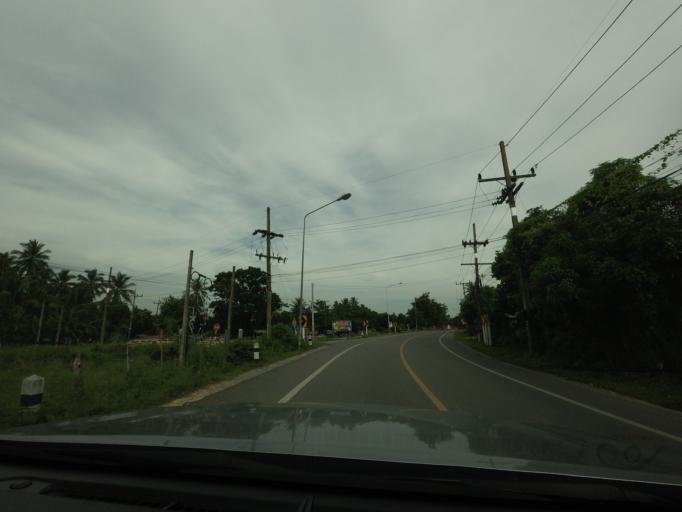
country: TH
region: Yala
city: Raman
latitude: 6.4526
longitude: 101.4491
